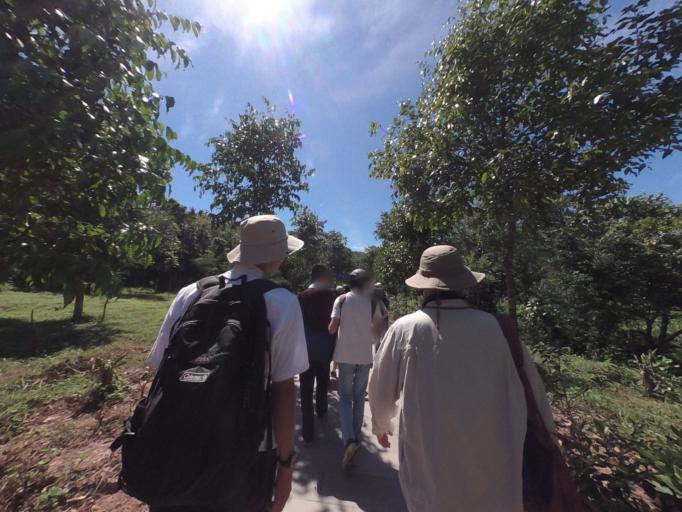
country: VN
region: Quang Nam
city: Dai Loc
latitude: 15.7653
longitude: 108.1238
